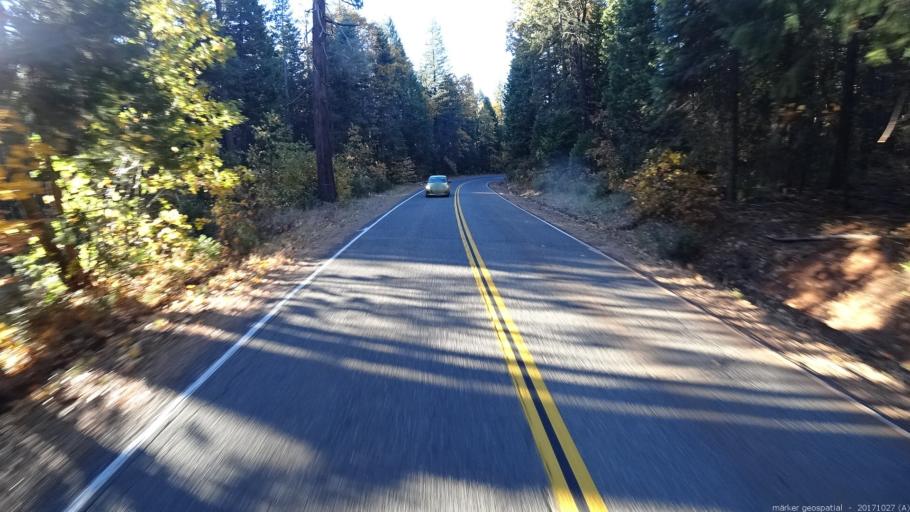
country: US
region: California
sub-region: Shasta County
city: Burney
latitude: 40.9698
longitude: -121.9295
